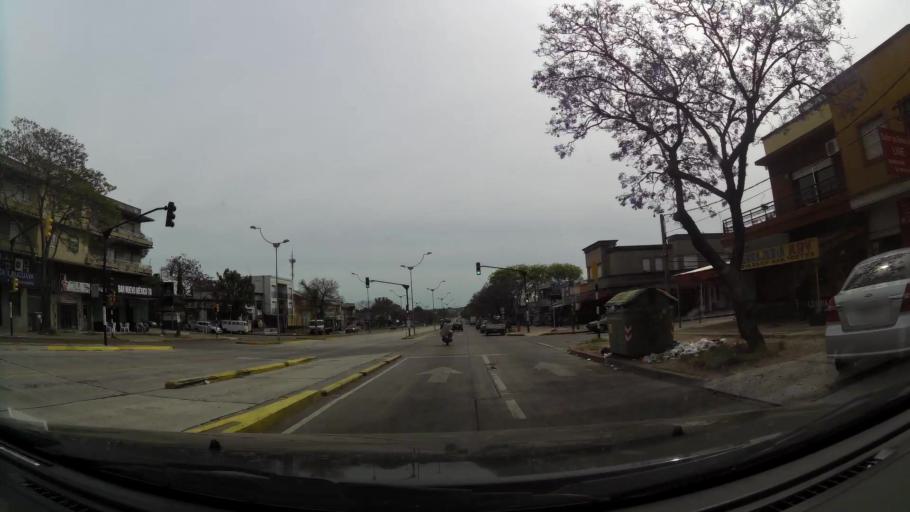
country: UY
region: Montevideo
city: Montevideo
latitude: -34.8534
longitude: -56.1611
